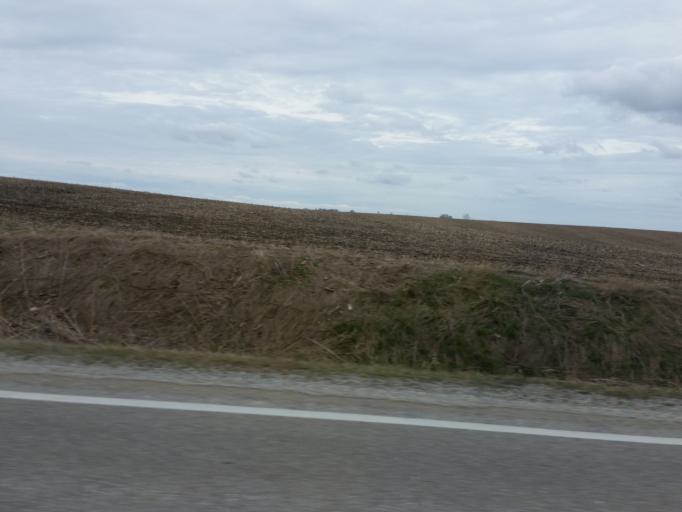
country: US
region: Iowa
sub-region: Black Hawk County
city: Waterloo
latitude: 42.5704
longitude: -92.3204
